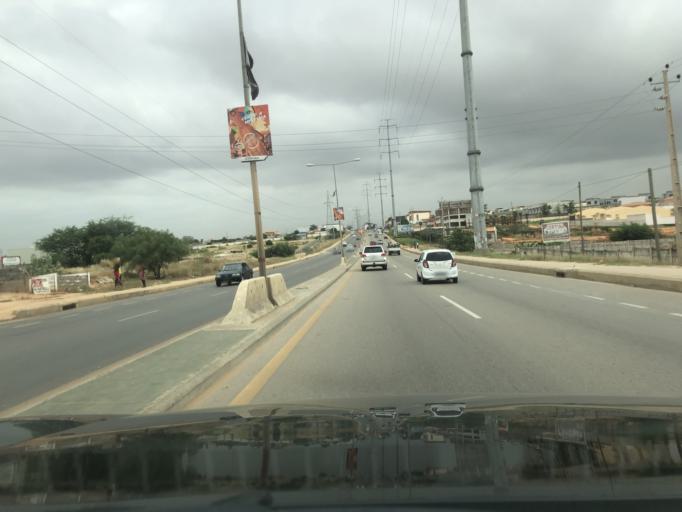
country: AO
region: Luanda
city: Luanda
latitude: -8.9682
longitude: 13.2070
